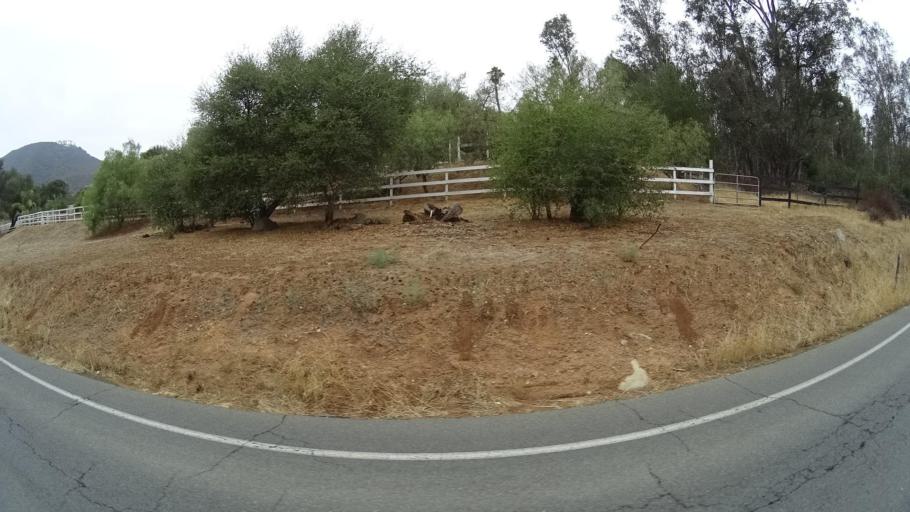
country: US
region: California
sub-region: San Diego County
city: San Marcos
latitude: 33.0754
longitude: -117.1619
